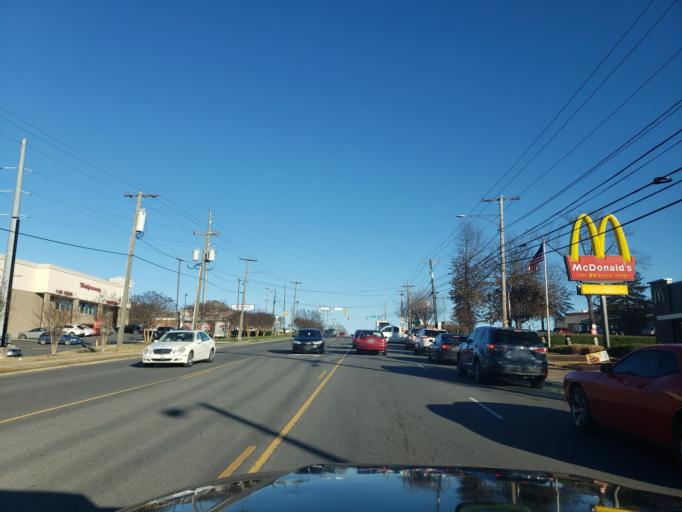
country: US
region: North Carolina
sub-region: Gaston County
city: Gastonia
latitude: 35.2596
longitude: -81.2174
